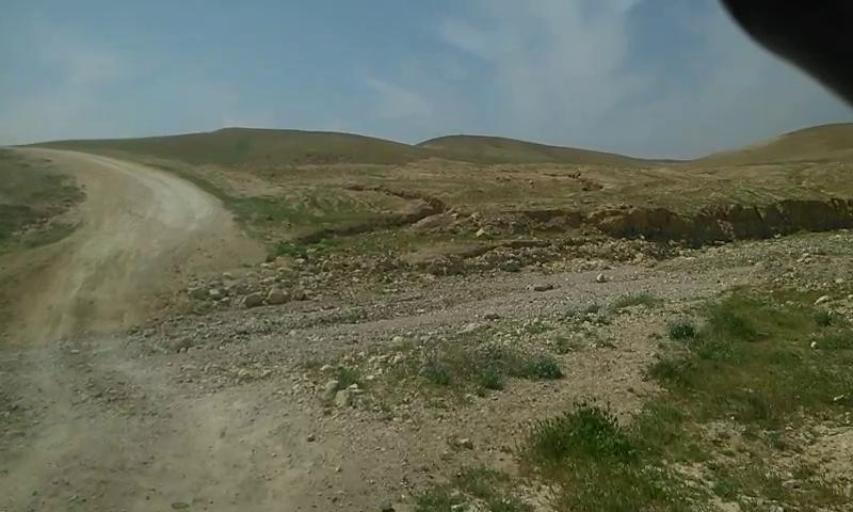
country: PS
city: `Arab ar Rashaydah
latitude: 31.4893
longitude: 35.2854
